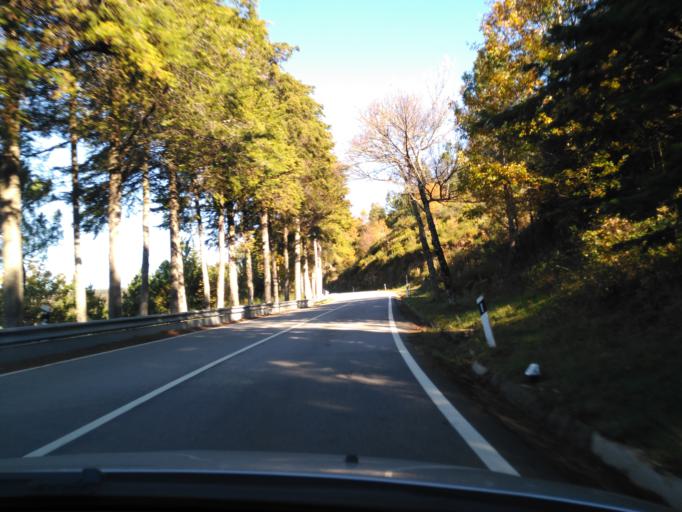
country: PT
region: Braga
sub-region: Cabeceiras de Basto
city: Cabeceiras de Basto
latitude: 41.6704
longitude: -7.9831
